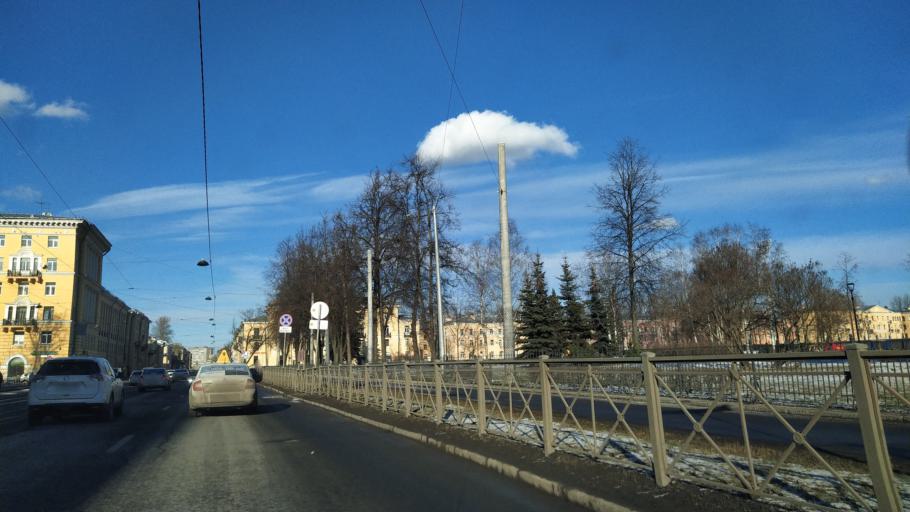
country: RU
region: Leningrad
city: Finlyandskiy
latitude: 59.9473
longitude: 30.4144
